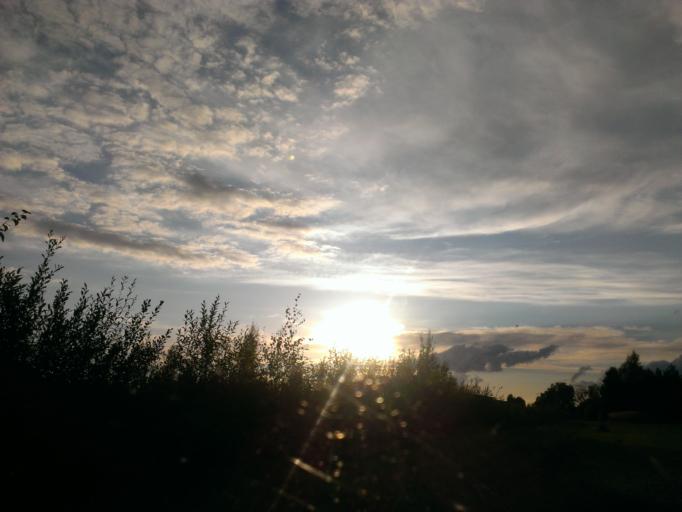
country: LV
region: Ikskile
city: Ikskile
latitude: 56.8346
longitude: 24.5256
